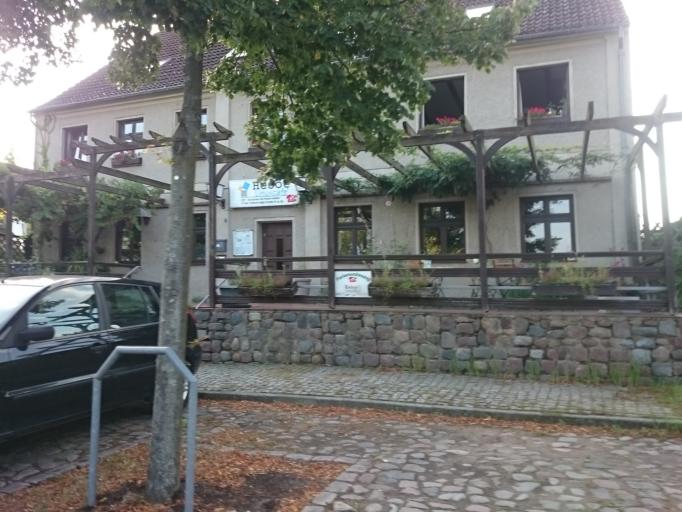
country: DE
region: Mecklenburg-Vorpommern
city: Neustrelitz
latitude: 53.2970
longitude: 13.0750
